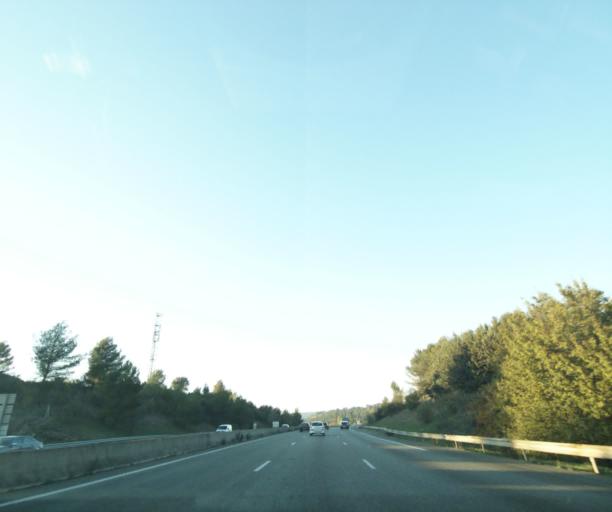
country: FR
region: Provence-Alpes-Cote d'Azur
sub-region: Departement des Bouches-du-Rhone
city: Meyreuil
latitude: 43.4885
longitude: 5.5297
